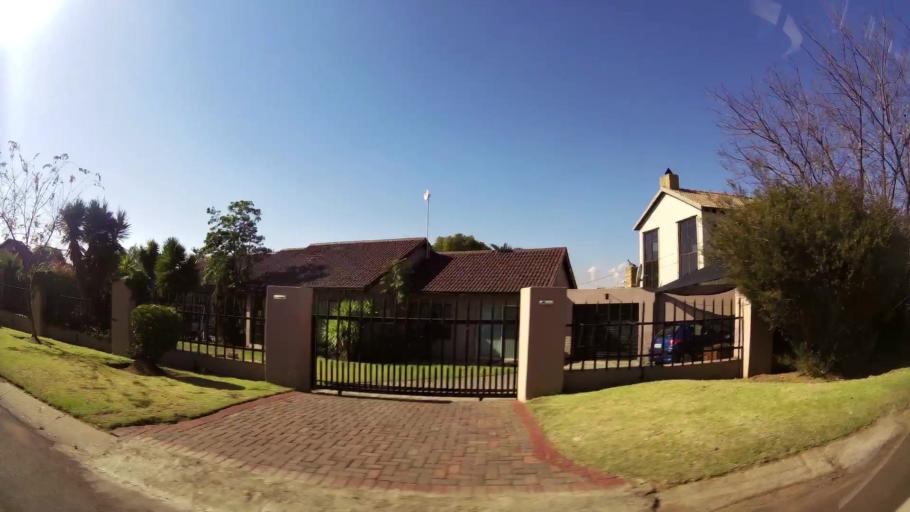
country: ZA
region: Mpumalanga
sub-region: Nkangala District Municipality
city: Witbank
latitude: -25.8749
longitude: 29.2452
